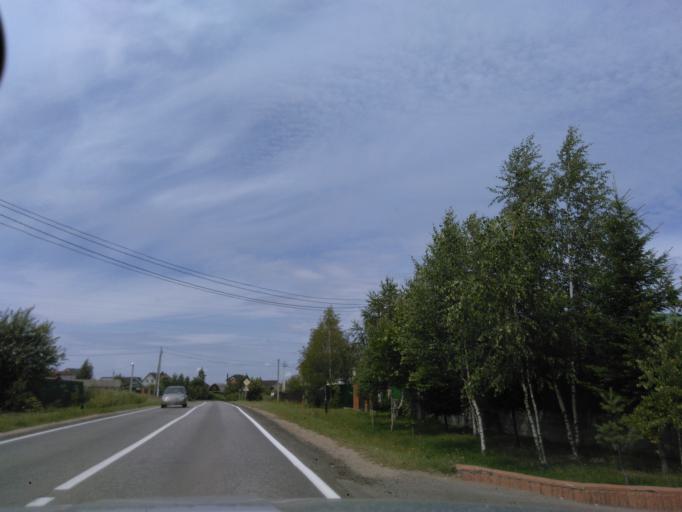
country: RU
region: Moskovskaya
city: Solnechnogorsk
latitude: 56.1586
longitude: 36.9796
